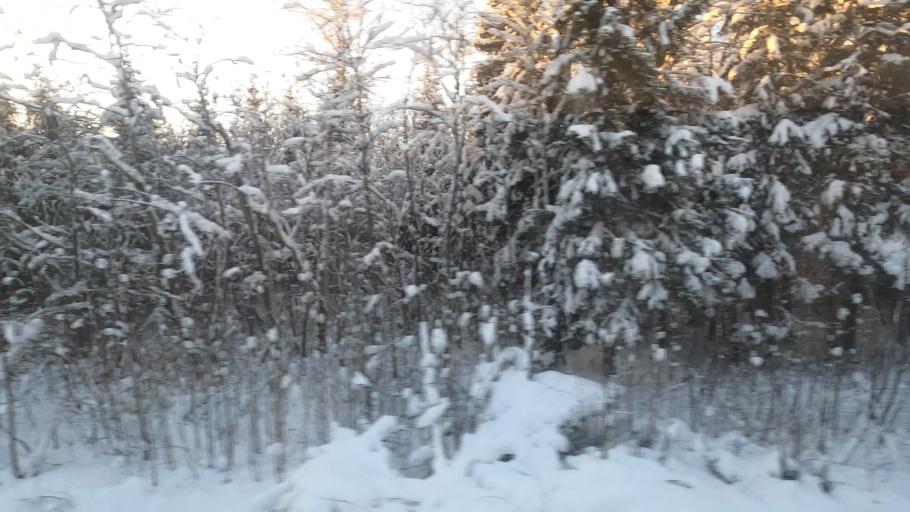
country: RU
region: Moskovskaya
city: Novo-Nikol'skoye
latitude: 56.5664
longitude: 37.5666
